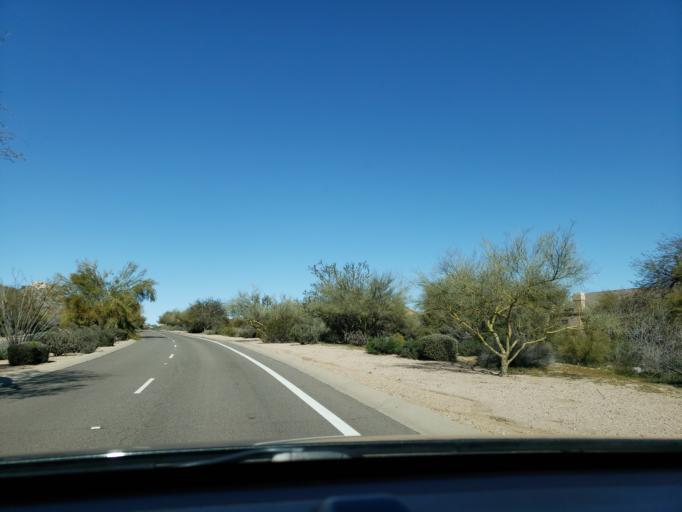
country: US
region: Arizona
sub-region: Maricopa County
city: Carefree
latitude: 33.7081
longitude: -111.8304
